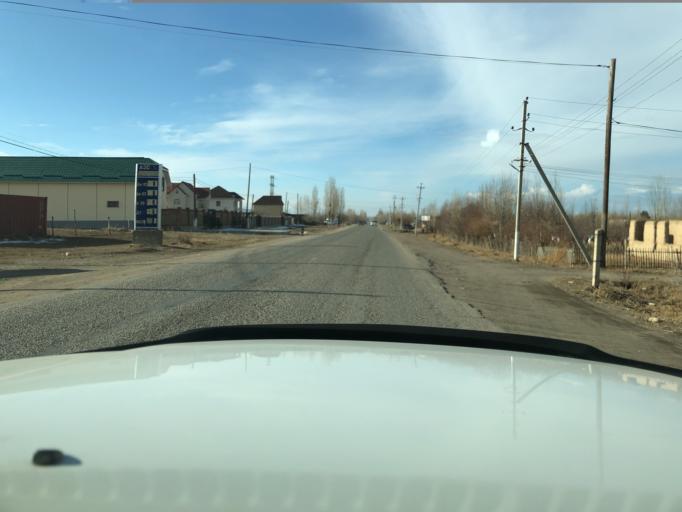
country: KG
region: Ysyk-Koel
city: Pokrovka
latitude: 42.3335
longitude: 77.9859
